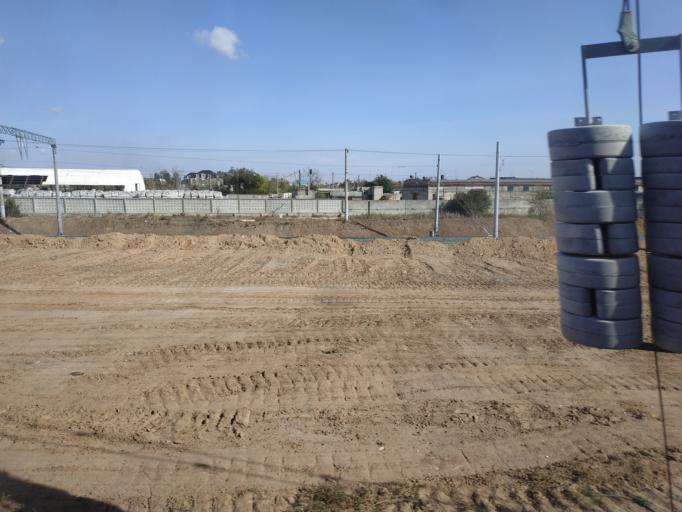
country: RU
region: Volgograd
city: Gumrak
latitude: 48.7726
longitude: 44.3852
